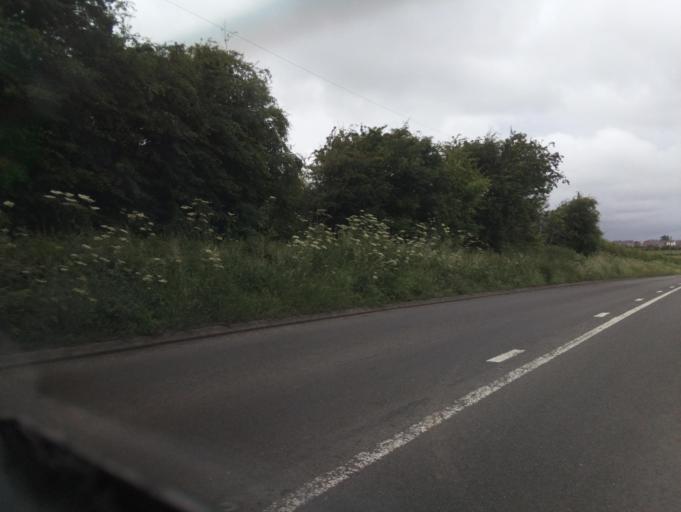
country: GB
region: England
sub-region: Staffordshire
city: Burton upon Trent
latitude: 52.8444
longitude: -1.6751
